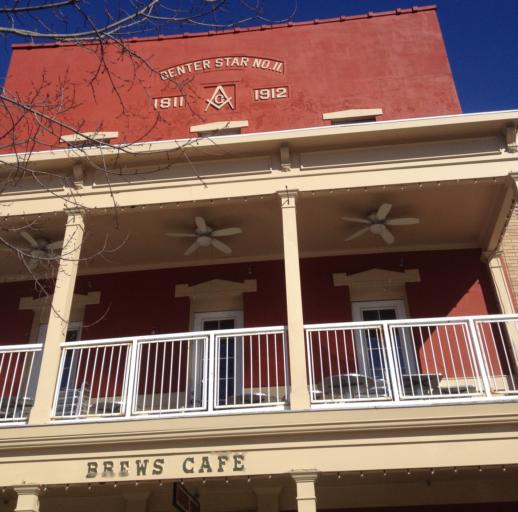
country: US
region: Ohio
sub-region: Licking County
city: Granville
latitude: 40.0681
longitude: -82.5195
